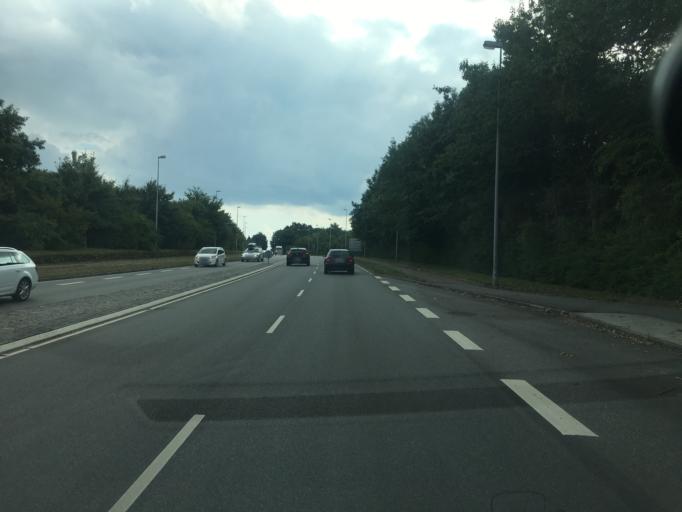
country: DK
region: South Denmark
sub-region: Sonderborg Kommune
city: Sonderborg
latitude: 54.9216
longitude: 9.7835
